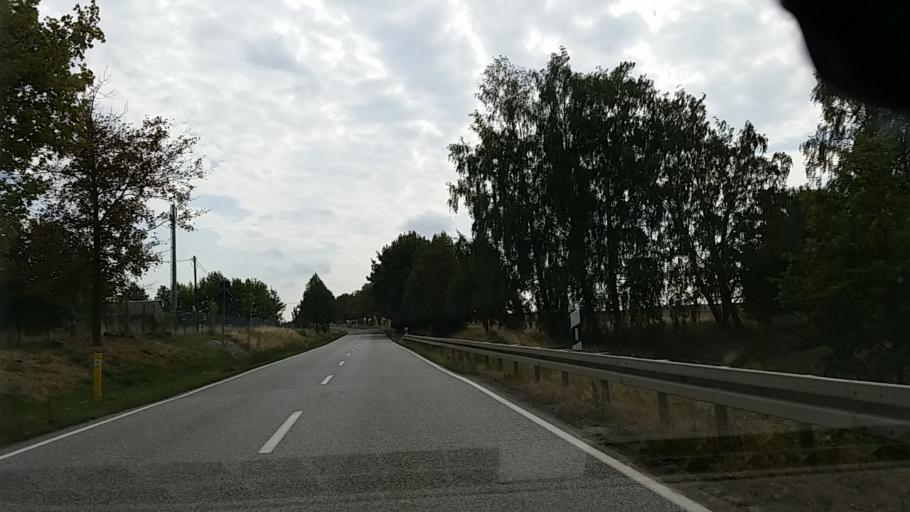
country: DE
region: Saxony-Anhalt
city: Nemsdorf-Gohrendorf
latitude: 51.3400
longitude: 11.6402
